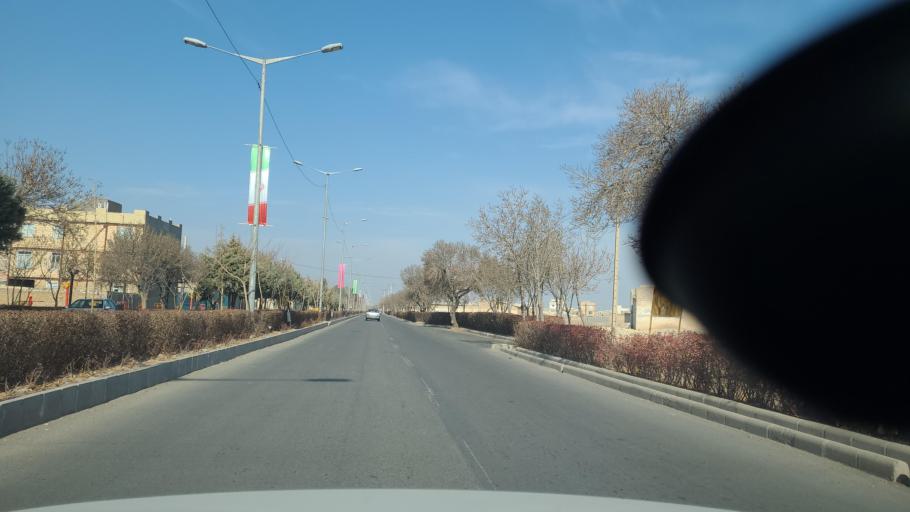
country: IR
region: Razavi Khorasan
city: Fariman
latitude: 35.6863
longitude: 59.8436
